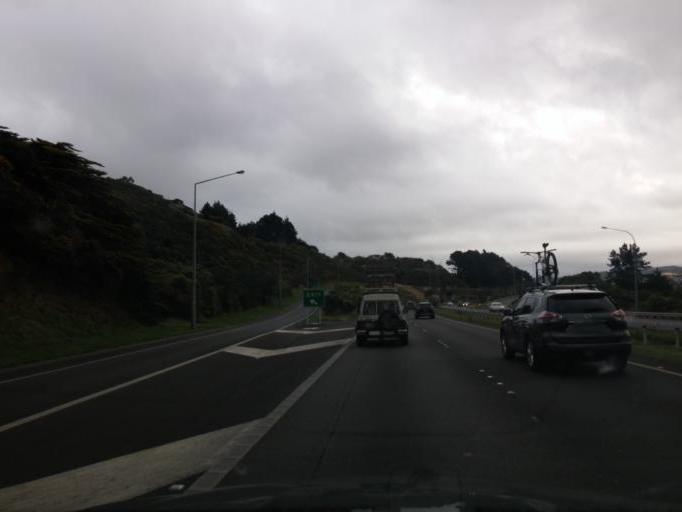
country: NZ
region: Wellington
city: Petone
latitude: -41.2020
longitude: 174.8230
